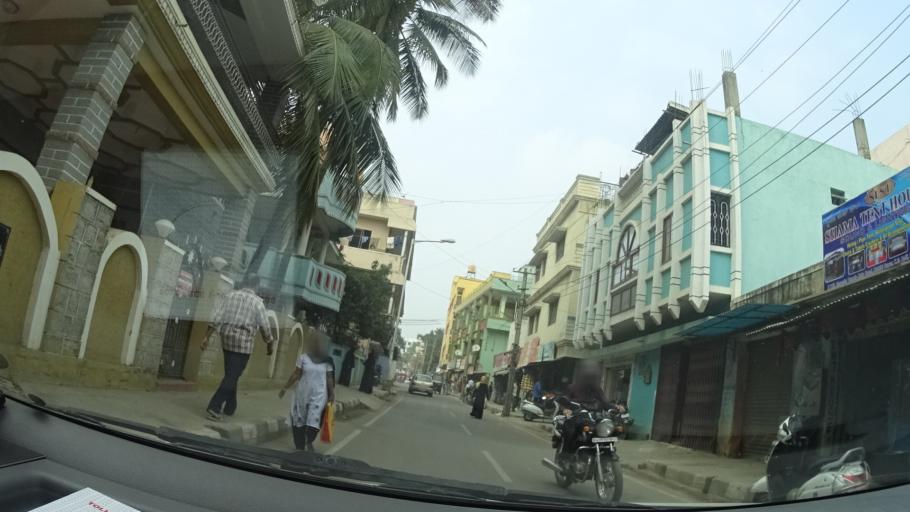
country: IN
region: Karnataka
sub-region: Bangalore Urban
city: Bangalore
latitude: 13.0217
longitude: 77.6213
